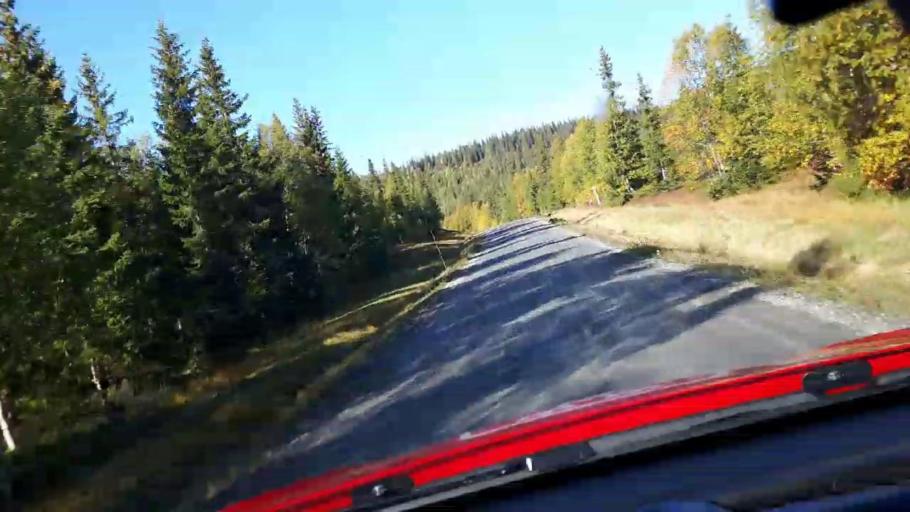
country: NO
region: Nord-Trondelag
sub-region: Lierne
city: Sandvika
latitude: 64.6110
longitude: 13.7346
